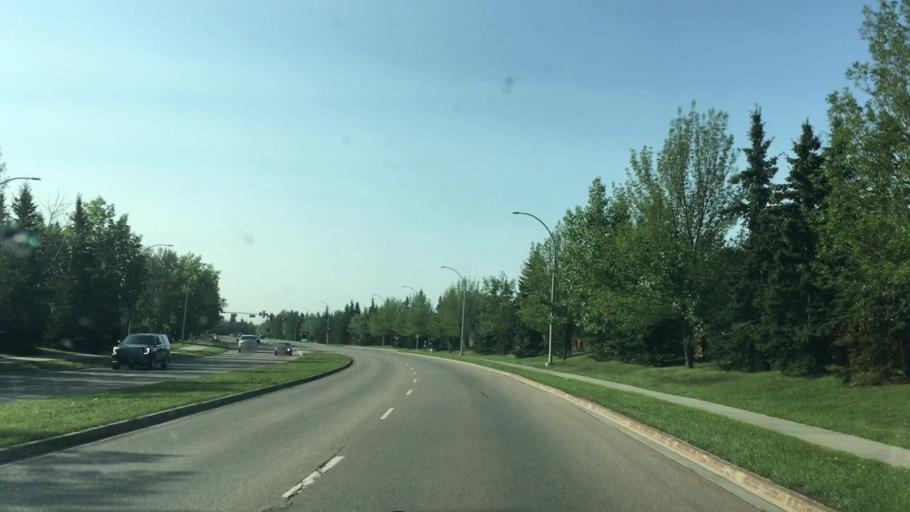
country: CA
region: Alberta
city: Edmonton
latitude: 53.4609
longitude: -113.5388
